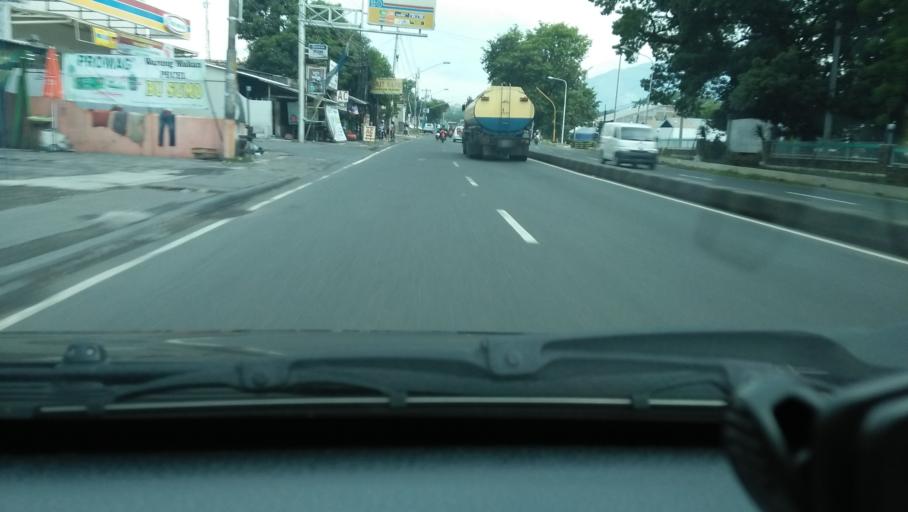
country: ID
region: Central Java
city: Ungaran
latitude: -7.0693
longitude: 110.4116
